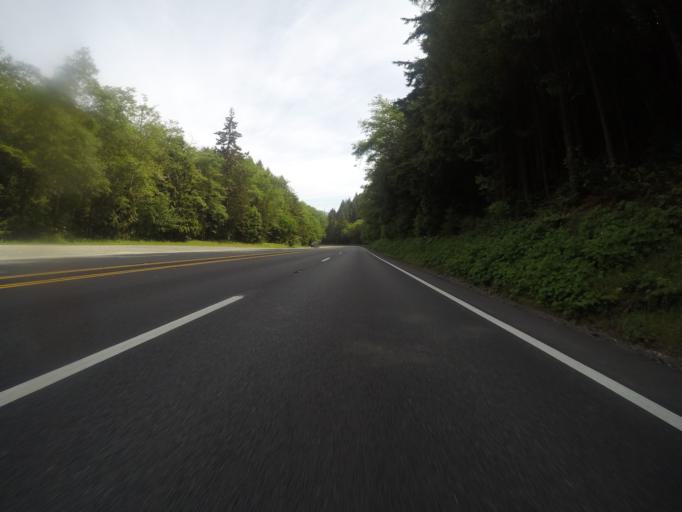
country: US
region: California
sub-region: Del Norte County
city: Bertsch-Oceanview
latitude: 41.4917
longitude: -124.0463
